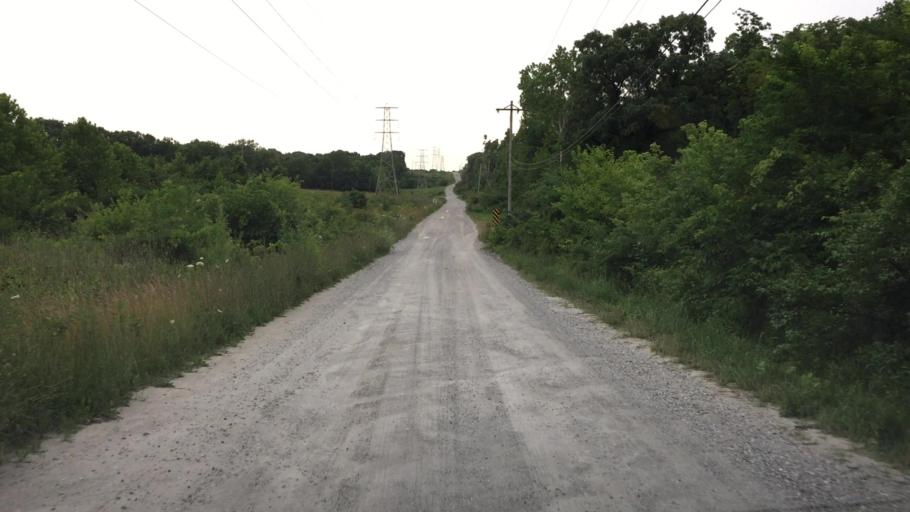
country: US
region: Illinois
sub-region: Hancock County
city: Hamilton
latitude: 40.3617
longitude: -91.3612
